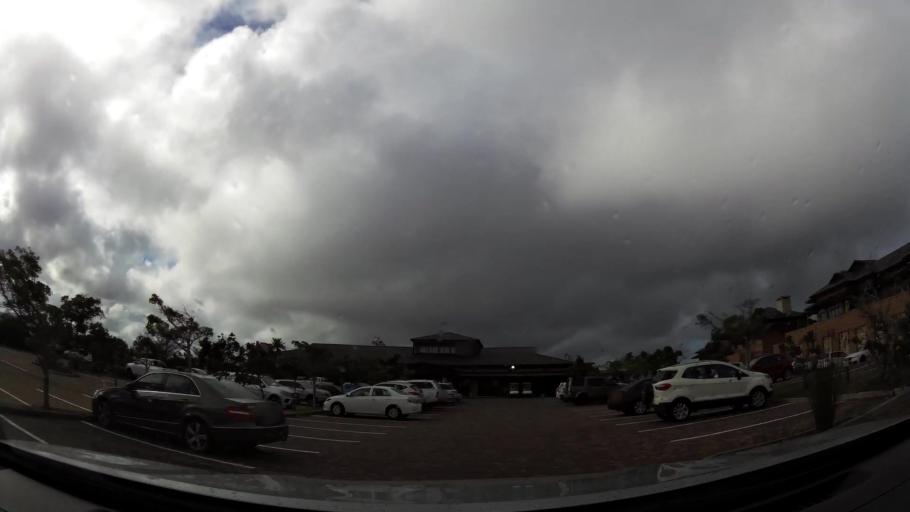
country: ZA
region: Western Cape
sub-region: Eden District Municipality
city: Knysna
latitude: -34.0697
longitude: 23.0895
